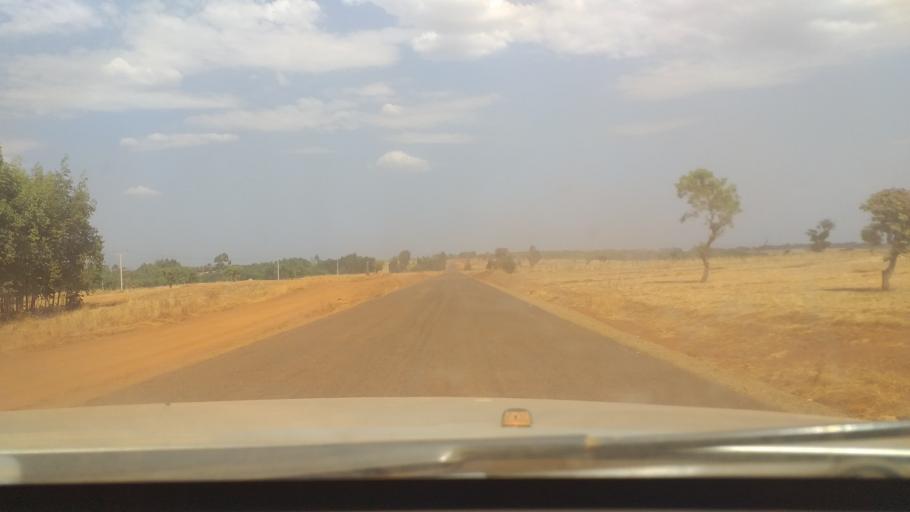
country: ET
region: Binshangul Gumuz
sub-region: Asosa
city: Asosa
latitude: 10.0784
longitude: 34.6418
